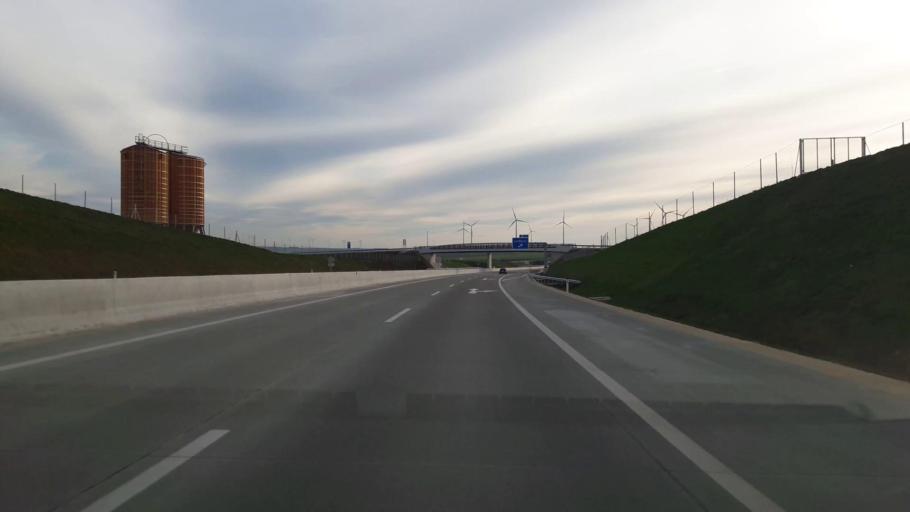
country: AT
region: Lower Austria
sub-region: Politischer Bezirk Mistelbach
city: Herrnbaumgarten
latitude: 48.6558
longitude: 16.6902
